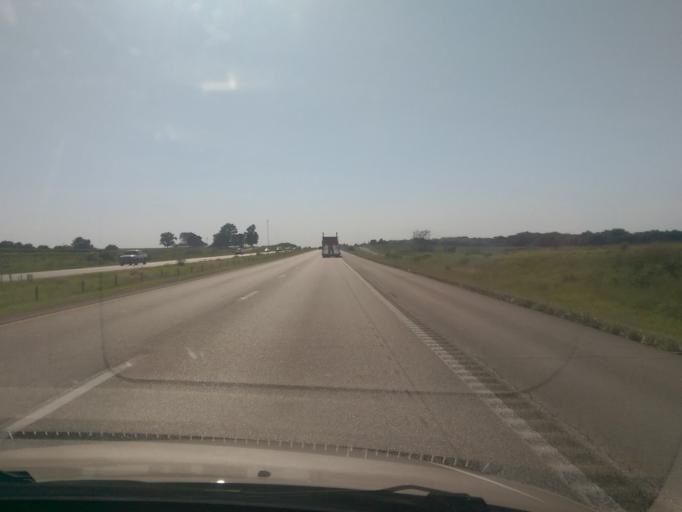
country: US
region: Missouri
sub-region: Saline County
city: Sweet Springs
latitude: 38.9755
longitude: -93.3809
